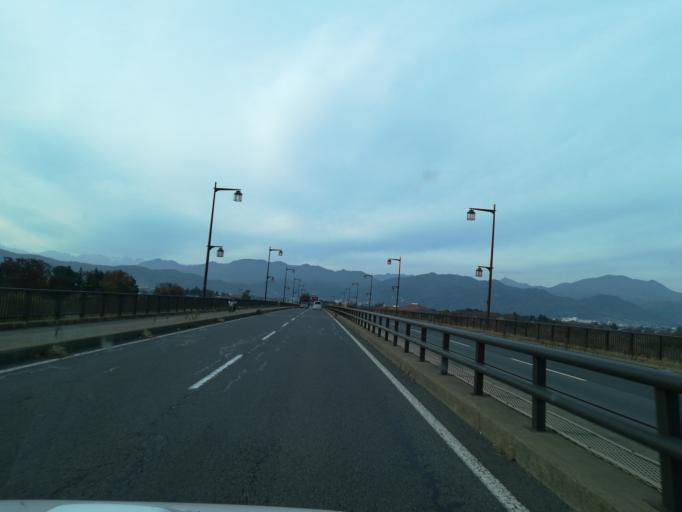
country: JP
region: Nagano
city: Nagano-shi
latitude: 36.5810
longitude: 138.1939
